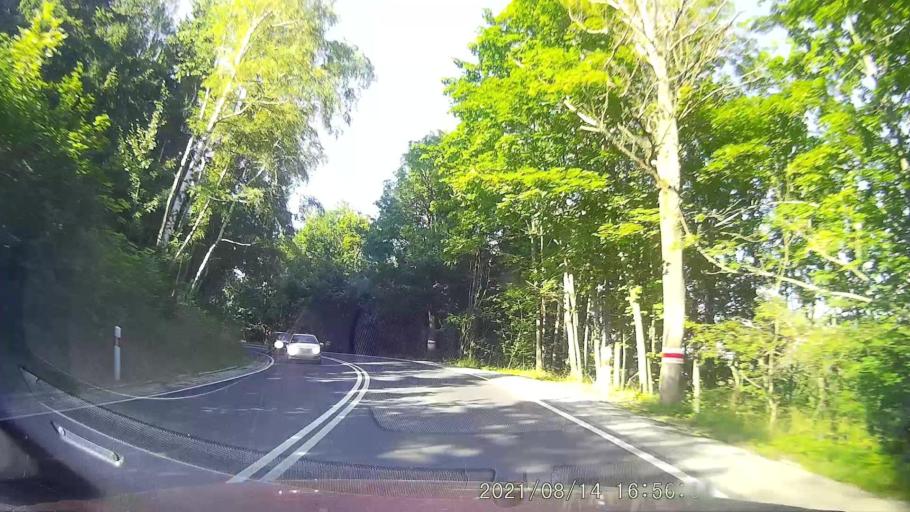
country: PL
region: Lower Silesian Voivodeship
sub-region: Powiat jeleniogorski
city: Kowary
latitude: 50.7545
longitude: 15.8675
